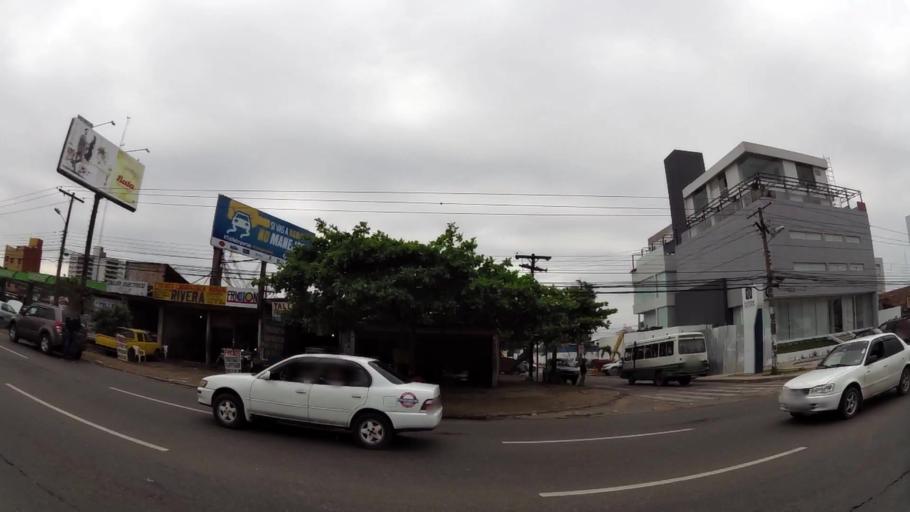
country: BO
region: Santa Cruz
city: Santa Cruz de la Sierra
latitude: -17.7757
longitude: -63.1654
